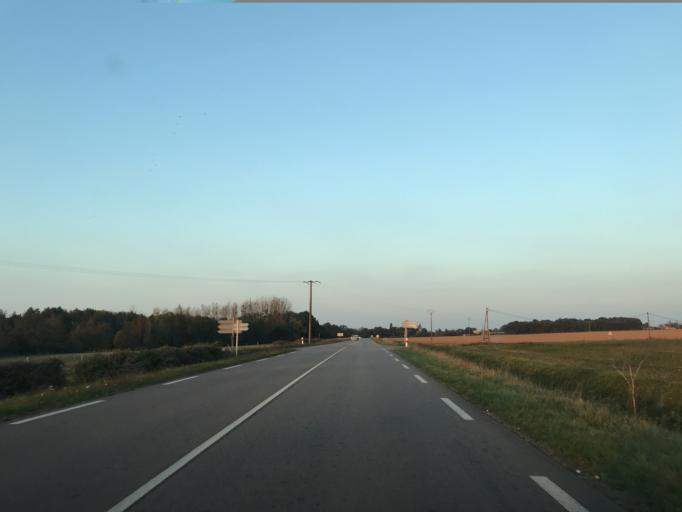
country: FR
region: Haute-Normandie
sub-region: Departement de l'Eure
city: Bourth
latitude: 48.6780
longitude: 0.7983
